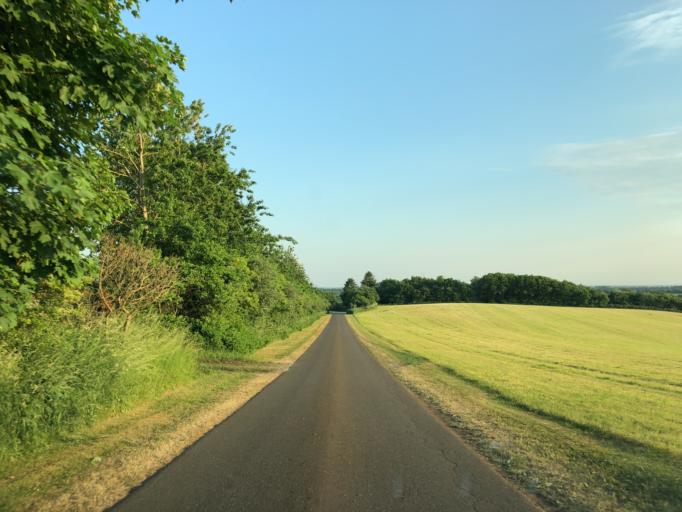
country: DK
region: Central Jutland
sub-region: Struer Kommune
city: Struer
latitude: 56.4064
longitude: 8.4878
